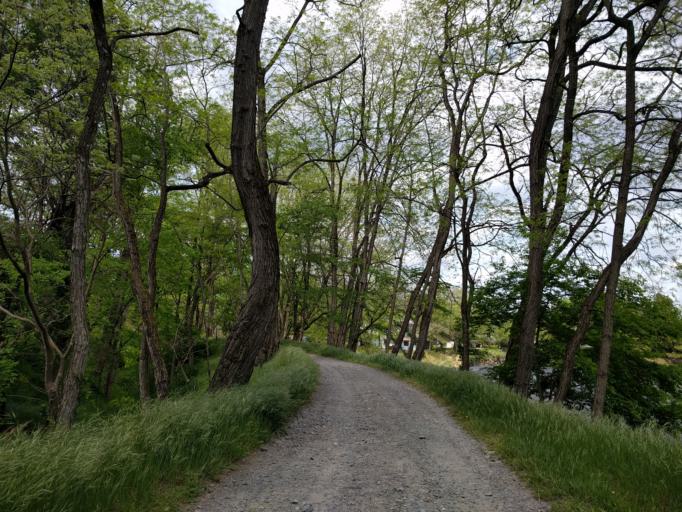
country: JP
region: Nagano
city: Hotaka
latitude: 36.3370
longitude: 137.9109
